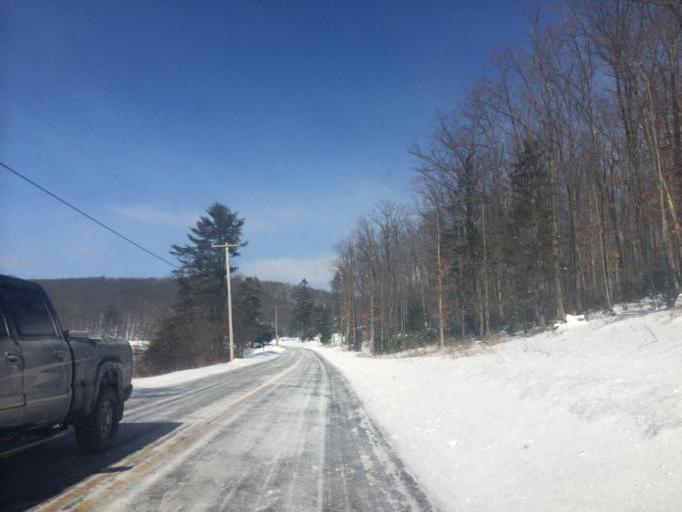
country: US
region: Pennsylvania
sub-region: Centre County
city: Stormstown
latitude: 40.9131
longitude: -78.0577
